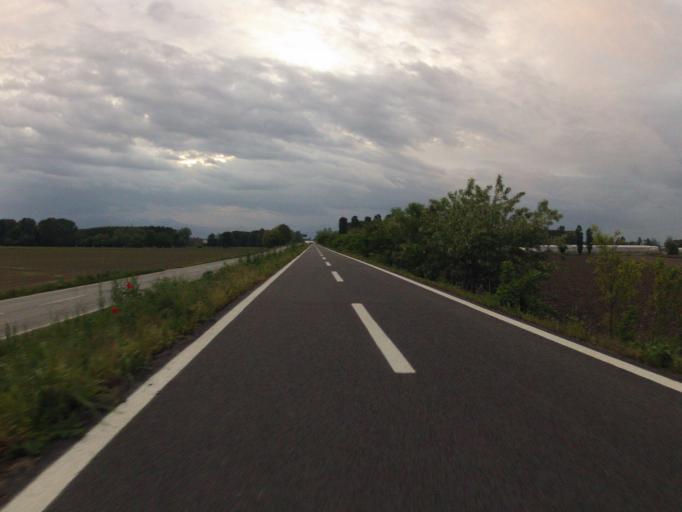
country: IT
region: Piedmont
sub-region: Provincia di Torino
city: Villafranca Piemonte
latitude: 44.7776
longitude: 7.5158
